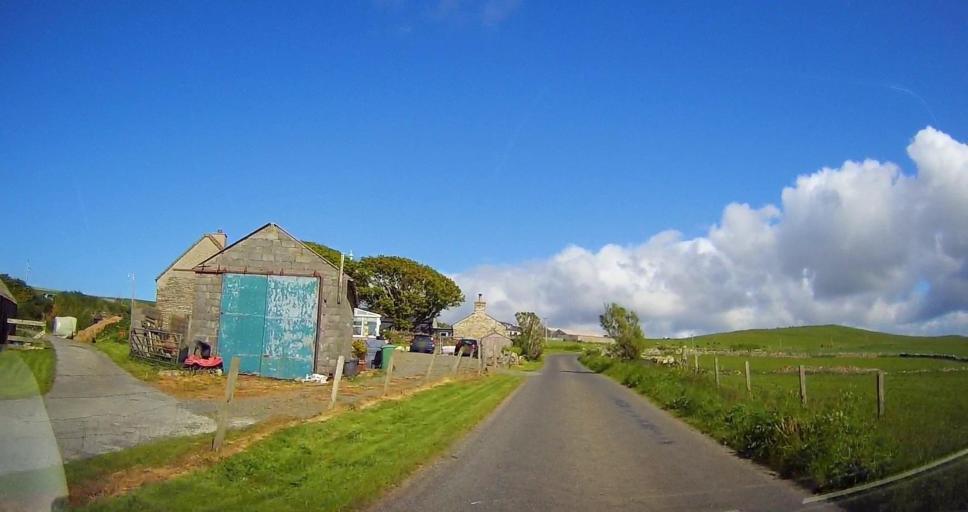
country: GB
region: Scotland
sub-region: Orkney Islands
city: Stromness
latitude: 58.9830
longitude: -3.1424
